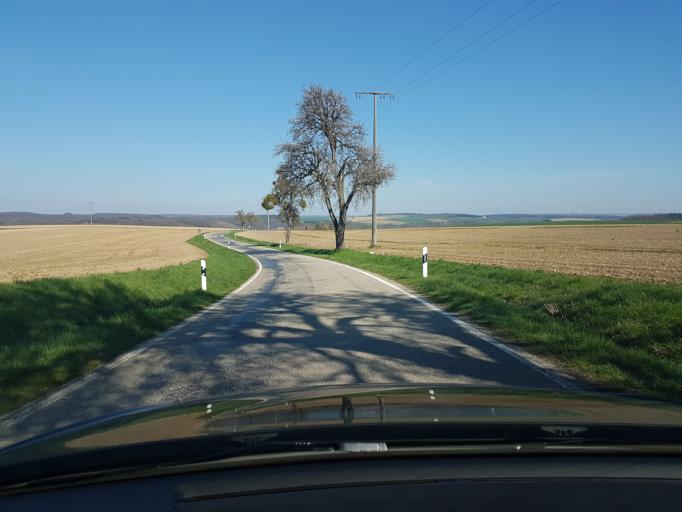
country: DE
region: Baden-Wuerttemberg
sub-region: Regierungsbezirk Stuttgart
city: Jagsthausen
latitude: 49.3184
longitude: 9.5138
